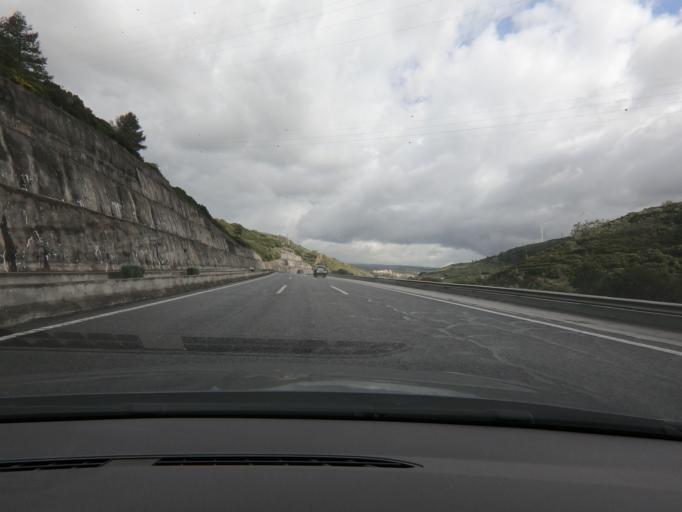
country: PT
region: Lisbon
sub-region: Loures
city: Bucelas
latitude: 38.8811
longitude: -9.1299
